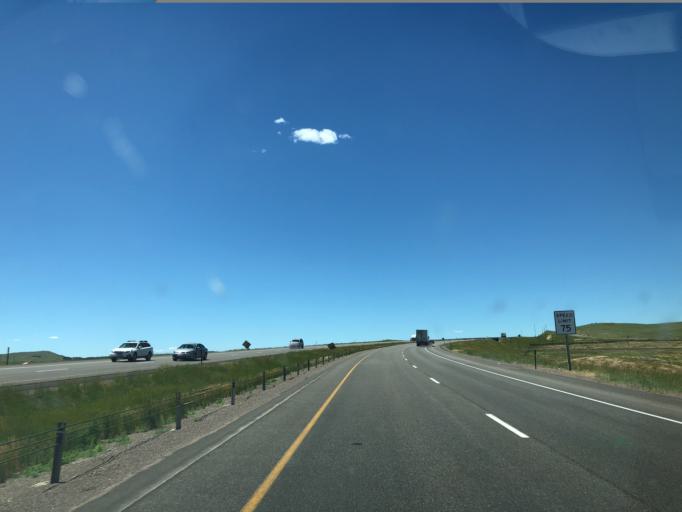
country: US
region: Wyoming
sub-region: Laramie County
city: Cheyenne
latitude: 41.0956
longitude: -105.2024
